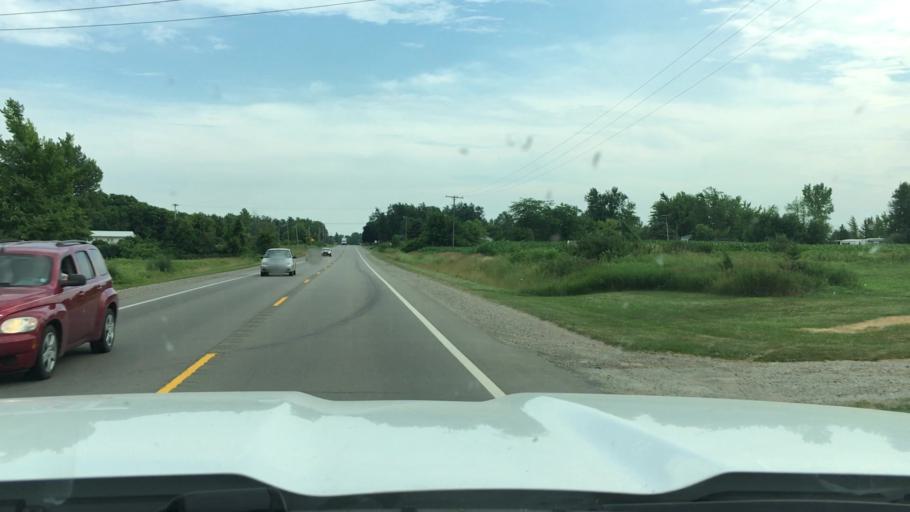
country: US
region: Michigan
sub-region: Sanilac County
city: Marlette
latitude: 43.3513
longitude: -83.0848
